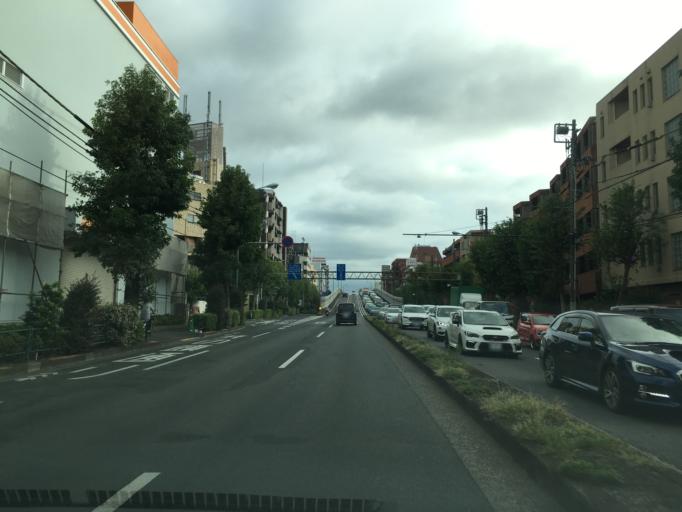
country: JP
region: Tokyo
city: Musashino
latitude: 35.6963
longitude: 139.6108
